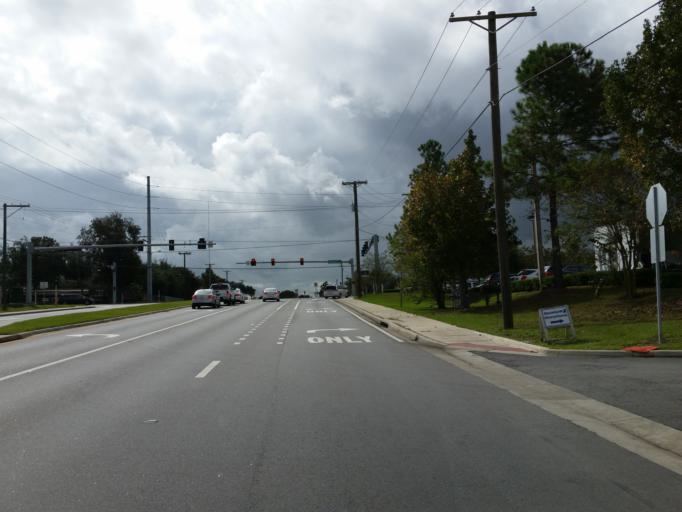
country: US
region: Florida
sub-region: Hillsborough County
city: Bloomingdale
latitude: 27.8547
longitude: -82.2693
